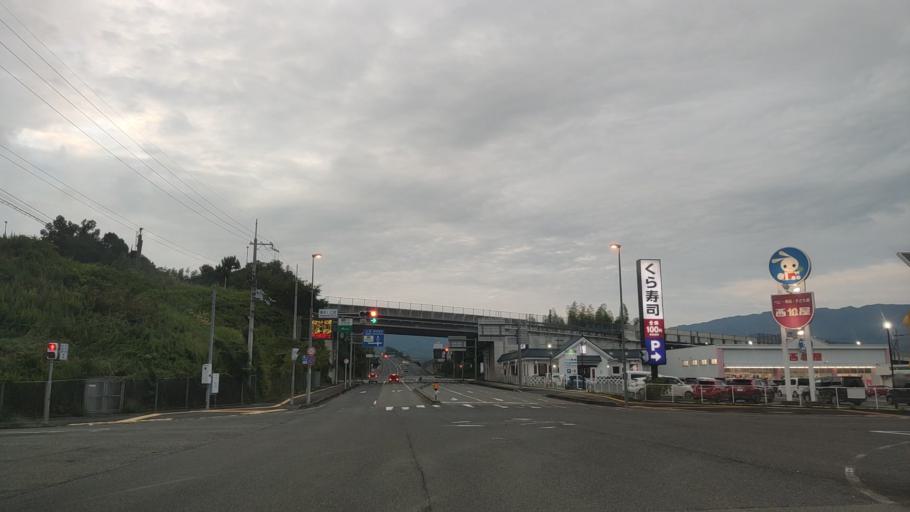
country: JP
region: Wakayama
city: Hashimoto
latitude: 34.3221
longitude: 135.6062
